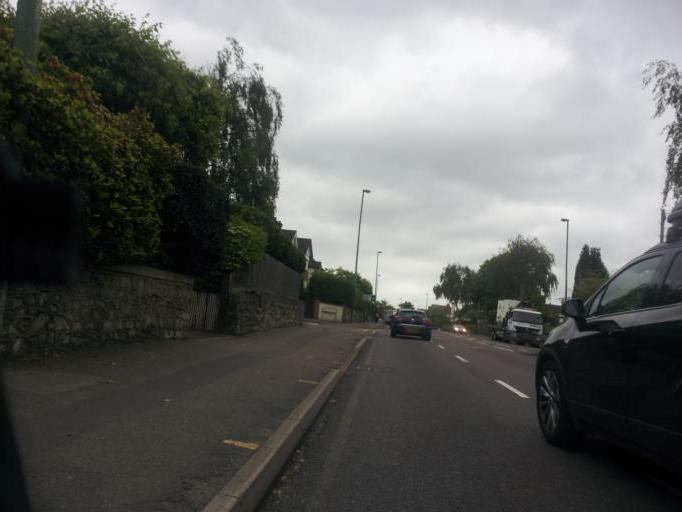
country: GB
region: England
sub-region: Kent
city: Maidstone
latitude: 51.2632
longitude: 0.5287
